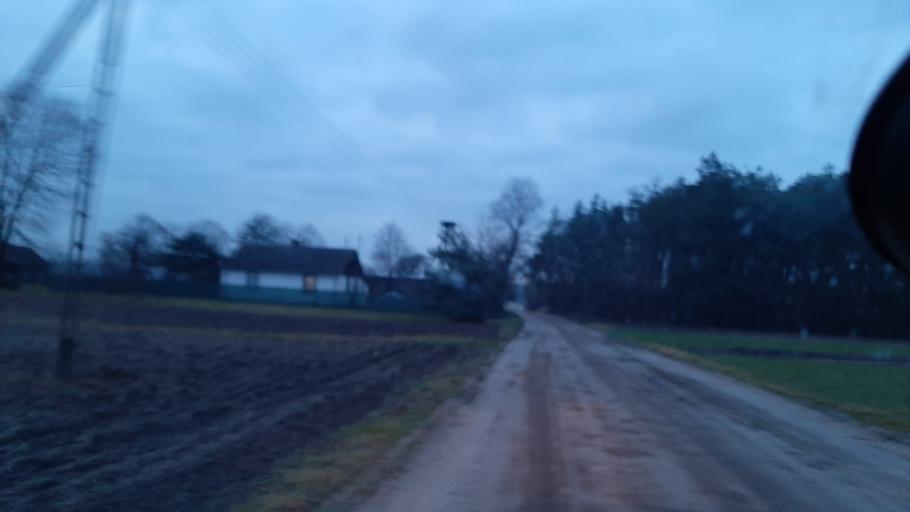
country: PL
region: Lublin Voivodeship
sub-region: Powiat lubartowski
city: Firlej
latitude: 51.5897
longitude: 22.5347
